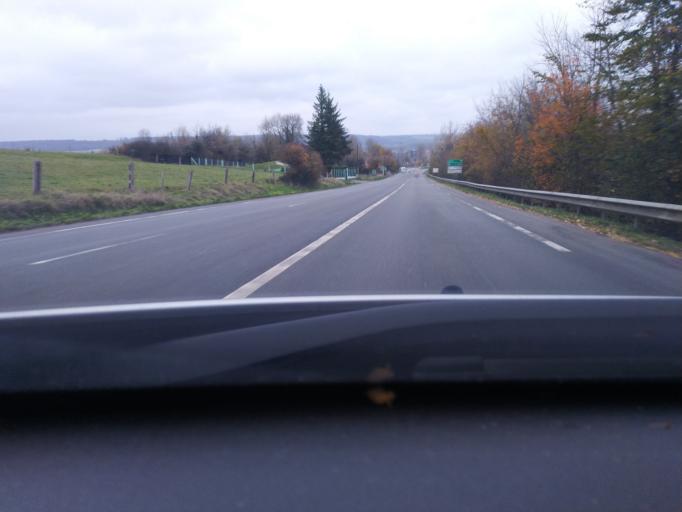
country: FR
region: Nord-Pas-de-Calais
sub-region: Departement du Pas-de-Calais
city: Hesdin
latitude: 50.3573
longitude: 2.0361
